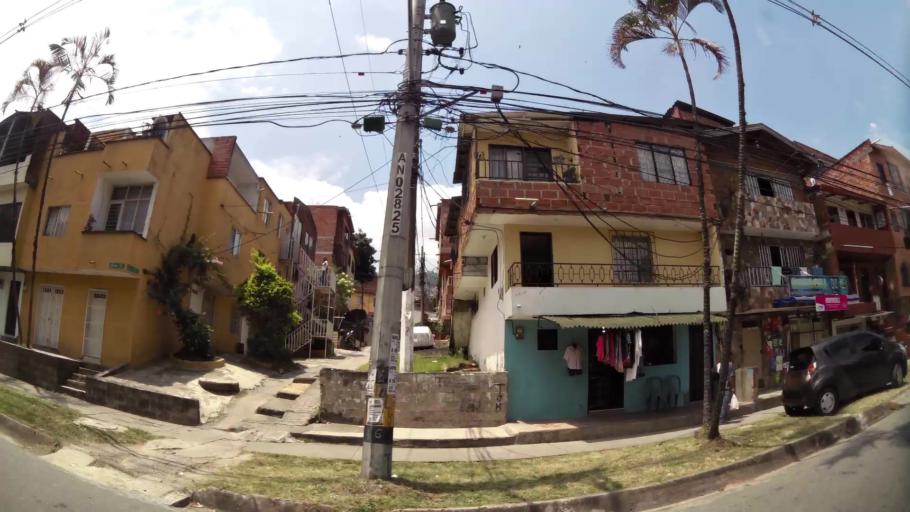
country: CO
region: Antioquia
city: Bello
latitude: 6.2974
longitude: -75.5760
